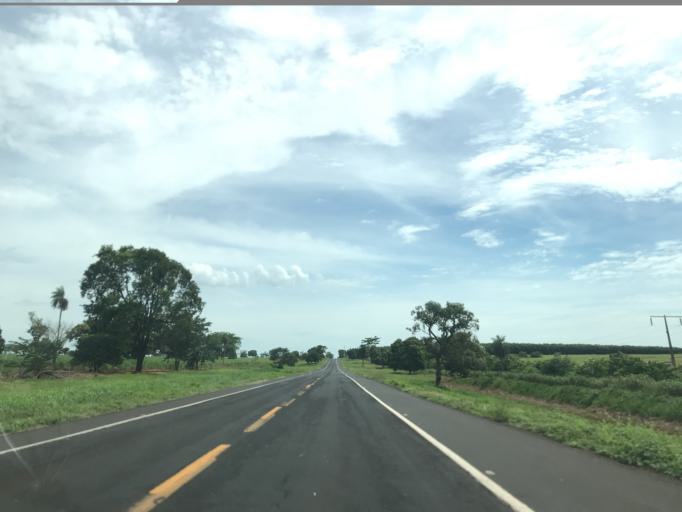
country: BR
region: Sao Paulo
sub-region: Nova Granada
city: Nova Granada
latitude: -20.4023
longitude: -49.2444
